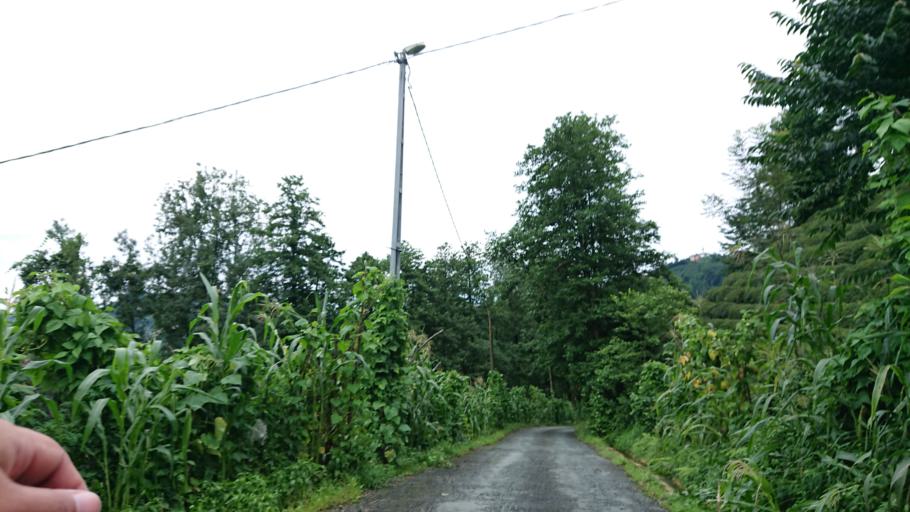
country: TR
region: Rize
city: Rize
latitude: 40.9859
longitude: 40.4847
